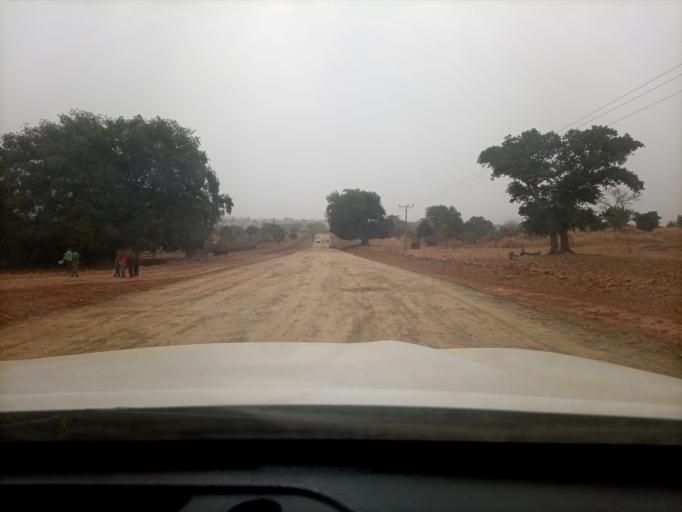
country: ET
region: Oromiya
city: Mendi
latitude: 10.1354
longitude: 35.1233
